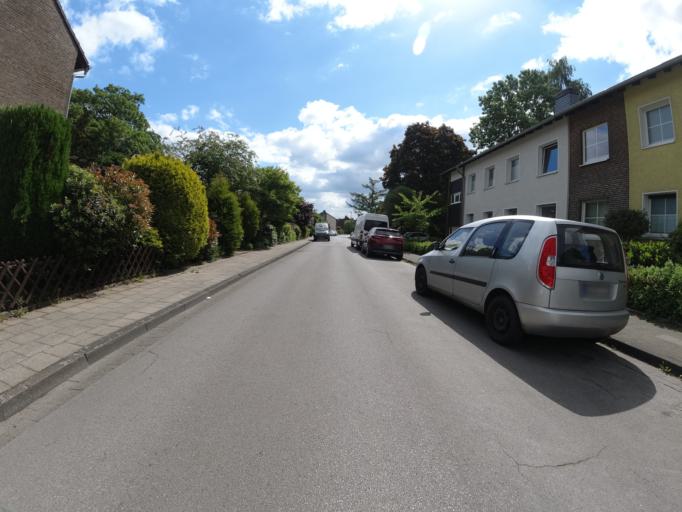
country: DE
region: North Rhine-Westphalia
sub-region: Regierungsbezirk Dusseldorf
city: Hochfeld
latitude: 51.3957
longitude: 6.7006
